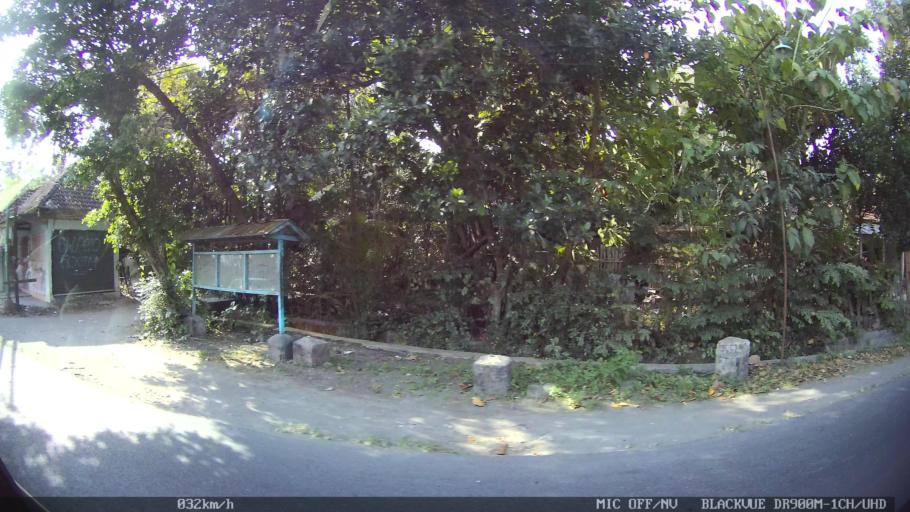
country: ID
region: Daerah Istimewa Yogyakarta
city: Pandak
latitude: -7.8932
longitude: 110.3006
